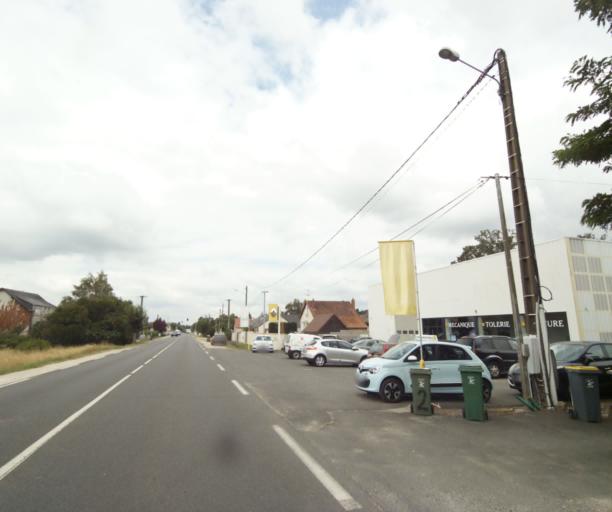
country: FR
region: Centre
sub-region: Departement du Loiret
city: Mardie
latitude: 47.8877
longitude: 2.0657
